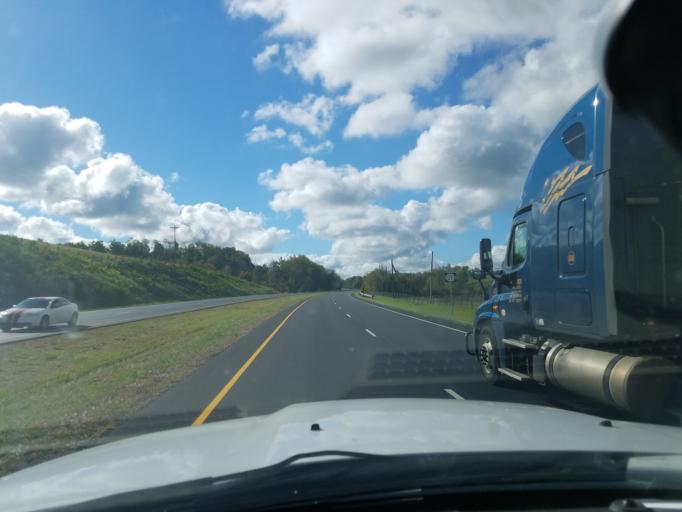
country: US
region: Kentucky
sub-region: Boyle County
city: Danville
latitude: 37.6072
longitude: -84.7275
